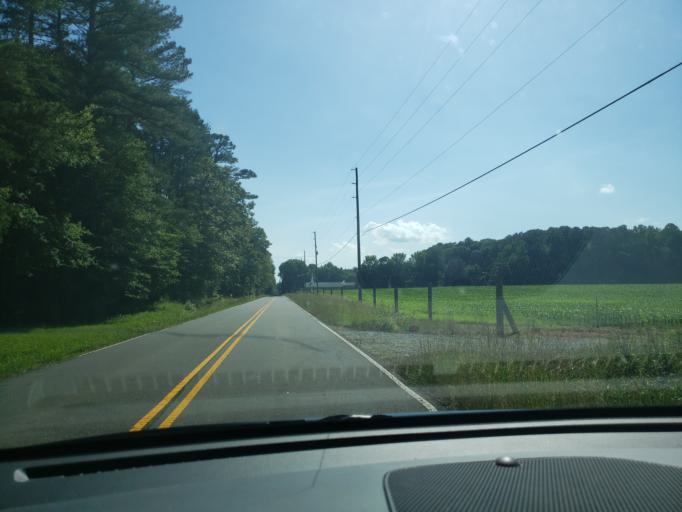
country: US
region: North Carolina
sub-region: Durham County
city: Gorman
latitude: 36.1246
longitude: -78.8916
